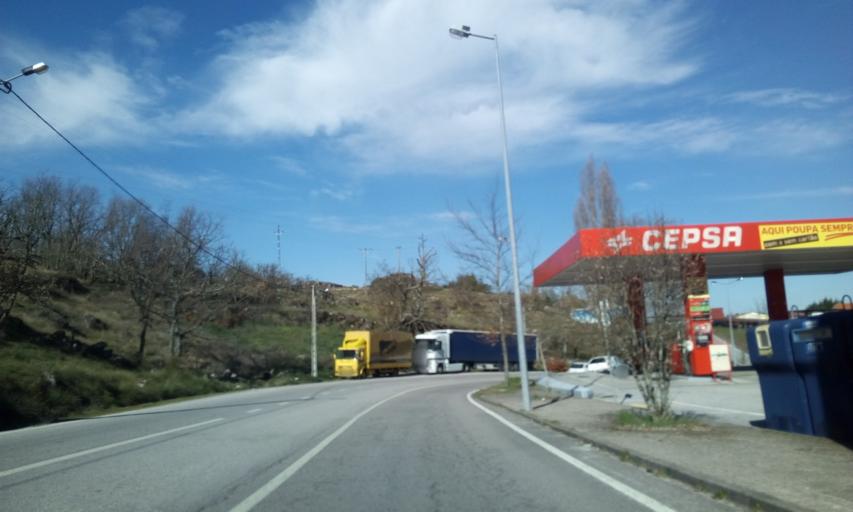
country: PT
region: Guarda
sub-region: Guarda
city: Sequeira
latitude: 40.5686
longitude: -7.2239
